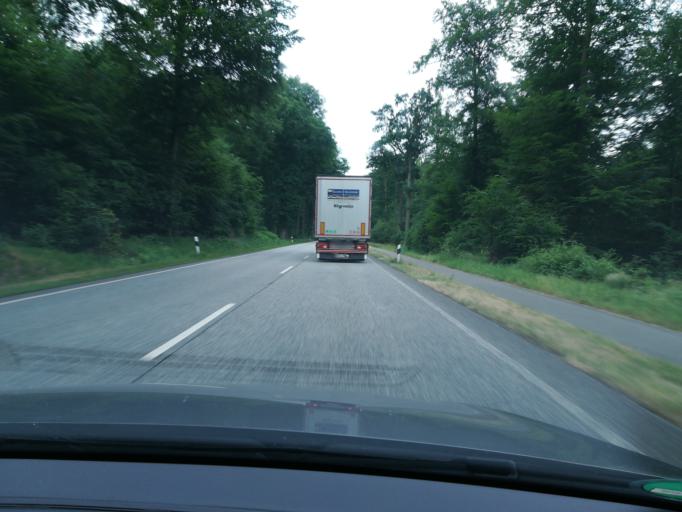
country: DE
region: Schleswig-Holstein
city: Kasseburg
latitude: 53.5454
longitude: 10.4198
